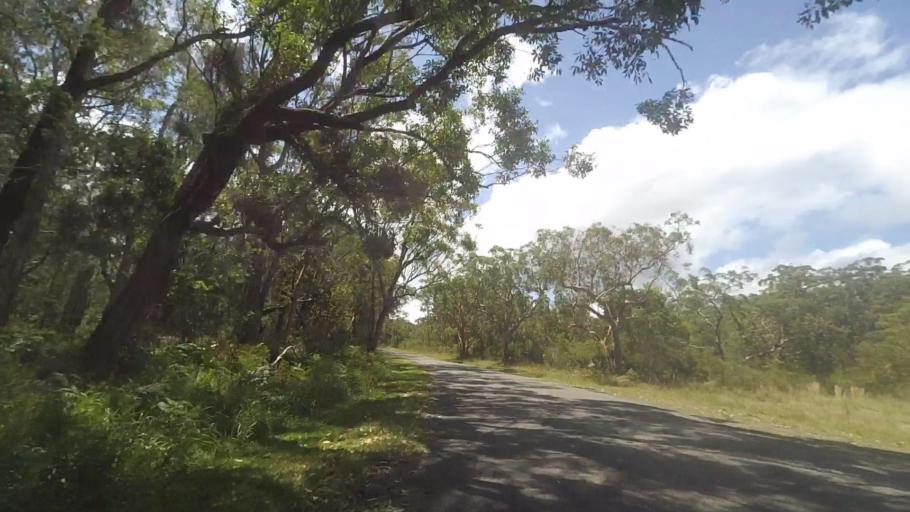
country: AU
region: New South Wales
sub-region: Great Lakes
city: Bulahdelah
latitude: -32.5160
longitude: 152.3230
